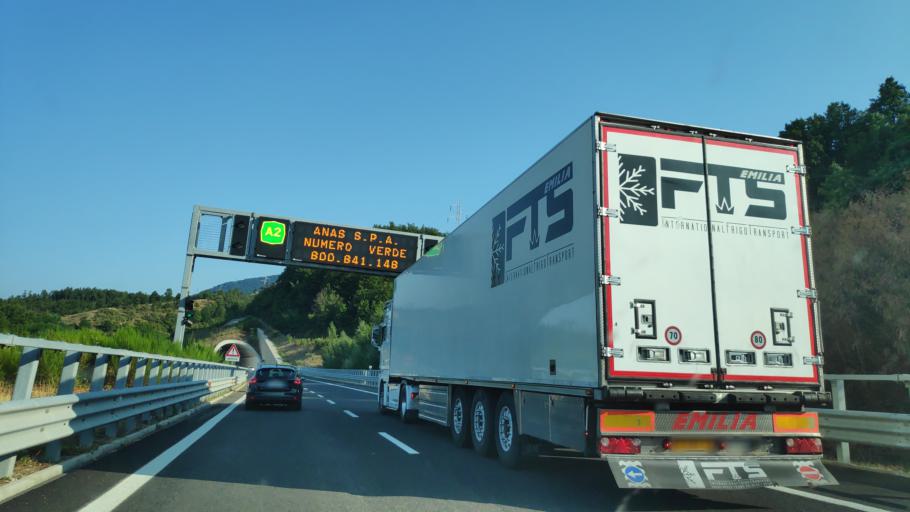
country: IT
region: Basilicate
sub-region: Provincia di Potenza
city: Lagonegro
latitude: 40.1076
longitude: 15.7945
